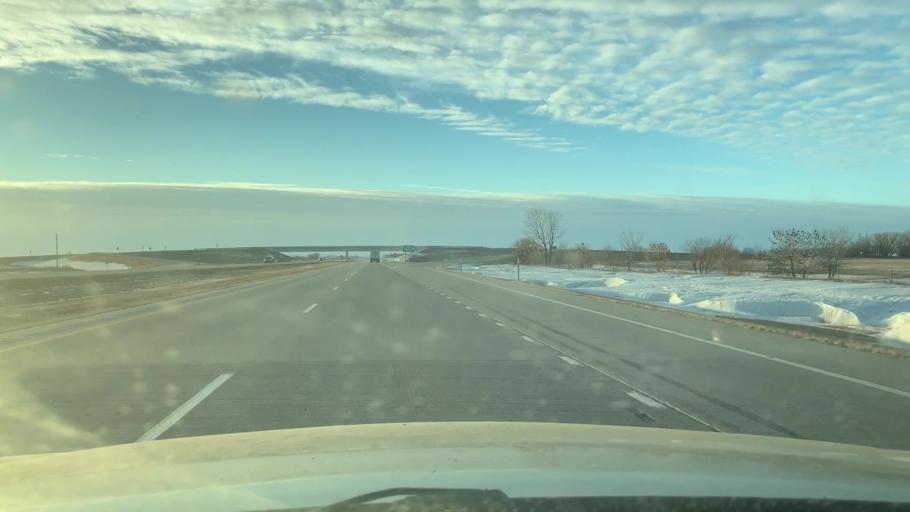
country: US
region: North Dakota
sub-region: Cass County
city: Casselton
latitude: 46.8758
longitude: -97.3400
